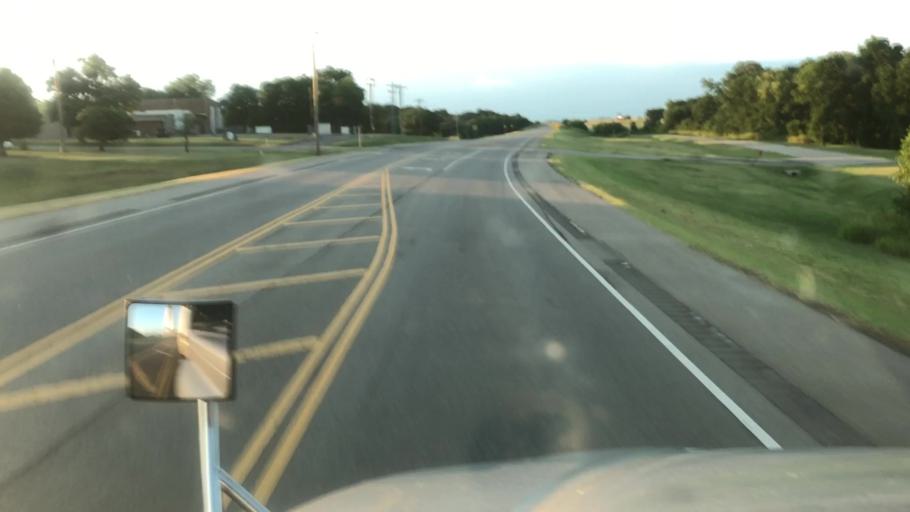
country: US
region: Oklahoma
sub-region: Osage County
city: McCord
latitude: 36.4902
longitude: -97.0734
